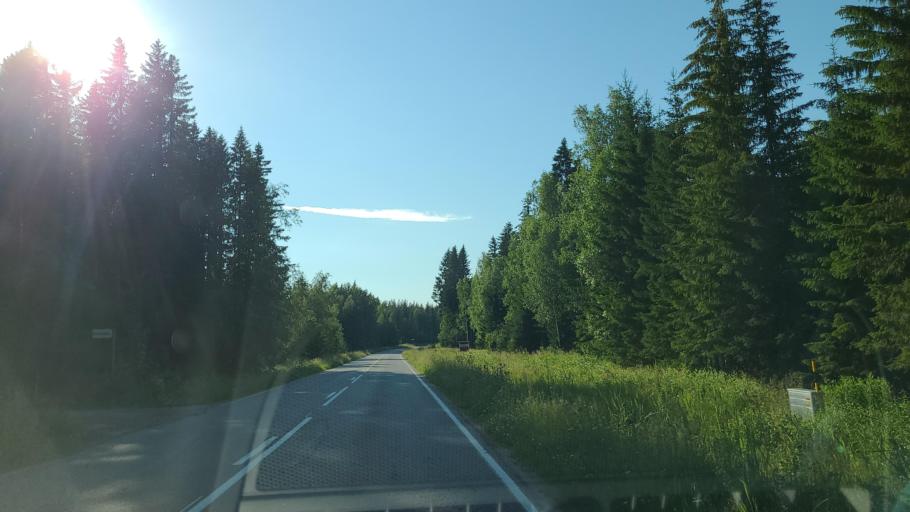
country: FI
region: Ostrobothnia
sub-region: Vaasa
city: Replot
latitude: 63.2377
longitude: 21.3914
